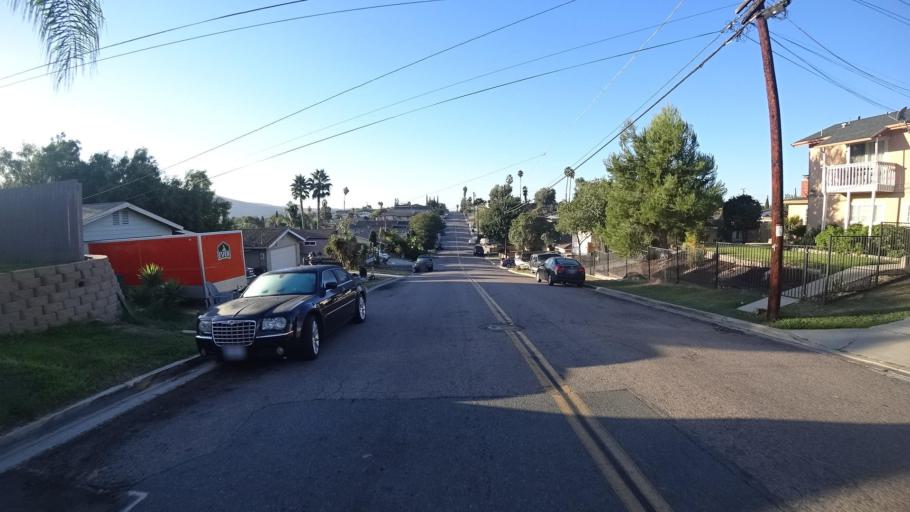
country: US
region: California
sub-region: San Diego County
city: La Presa
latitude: 32.7129
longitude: -116.9940
